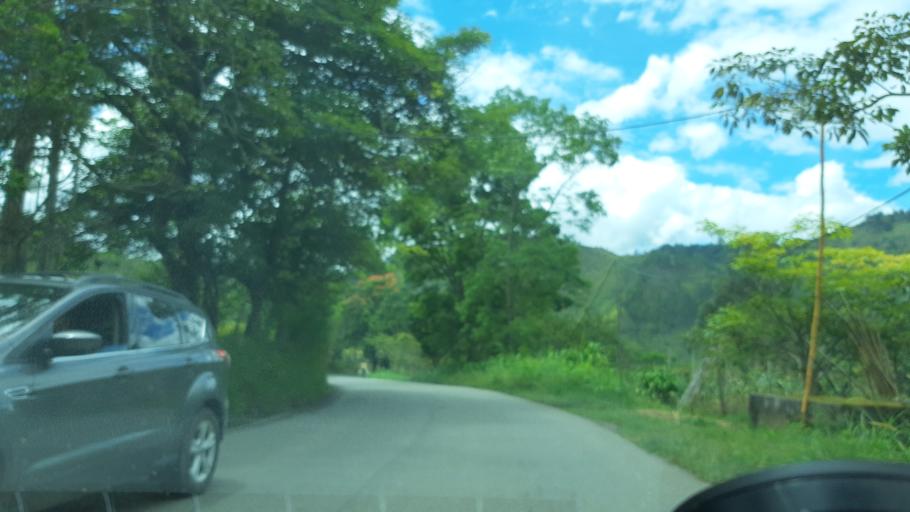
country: CO
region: Cundinamarca
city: Tenza
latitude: 5.0384
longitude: -73.3892
